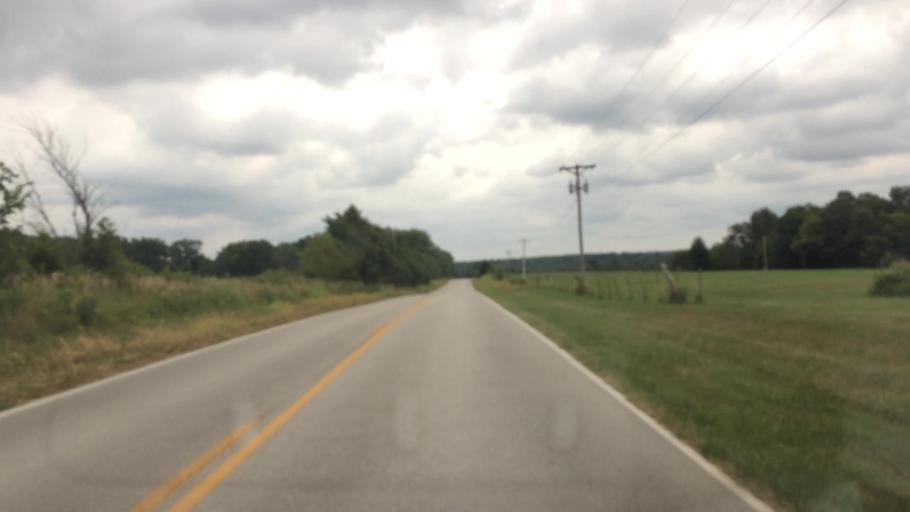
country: US
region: Missouri
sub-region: Greene County
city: Strafford
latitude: 37.2850
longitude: -93.1029
